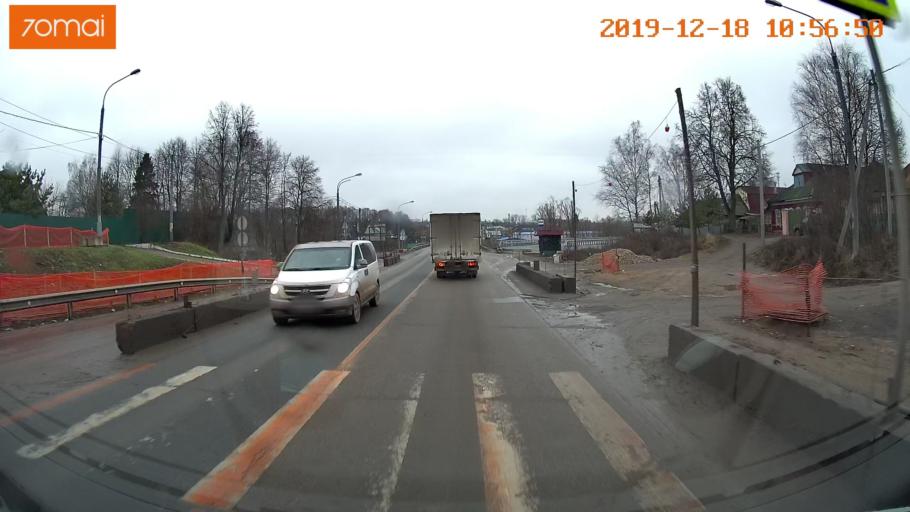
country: RU
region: Moskovskaya
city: Selyatino
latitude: 55.5435
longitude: 36.9875
